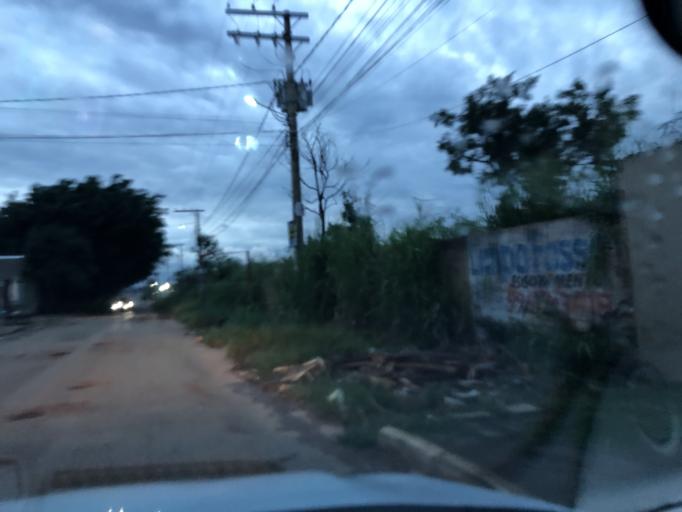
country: BR
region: Goias
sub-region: Luziania
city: Luziania
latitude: -16.1112
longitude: -47.9855
